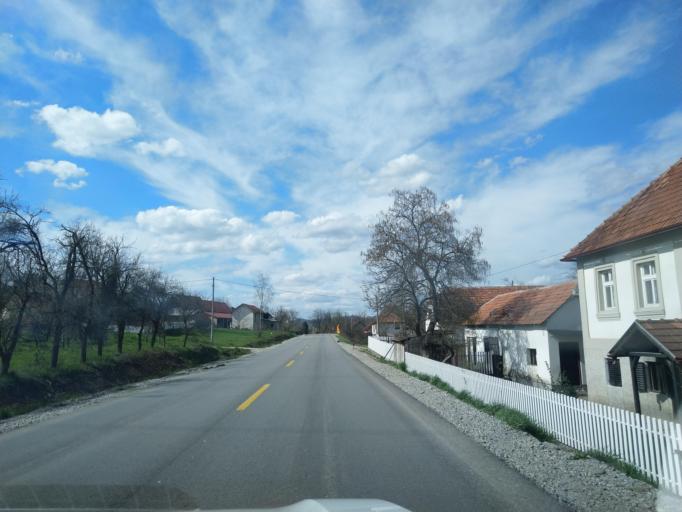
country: RS
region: Central Serbia
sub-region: Zlatiborski Okrug
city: Pozega
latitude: 43.8205
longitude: 20.0848
